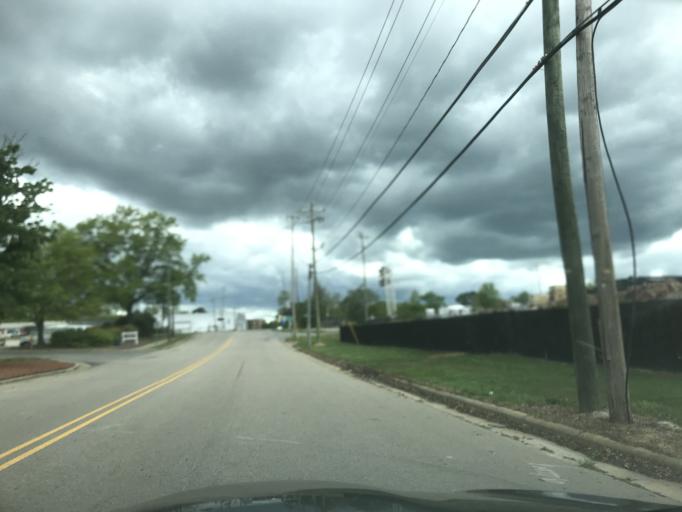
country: US
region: North Carolina
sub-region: Wake County
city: West Raleigh
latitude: 35.7894
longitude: -78.7140
